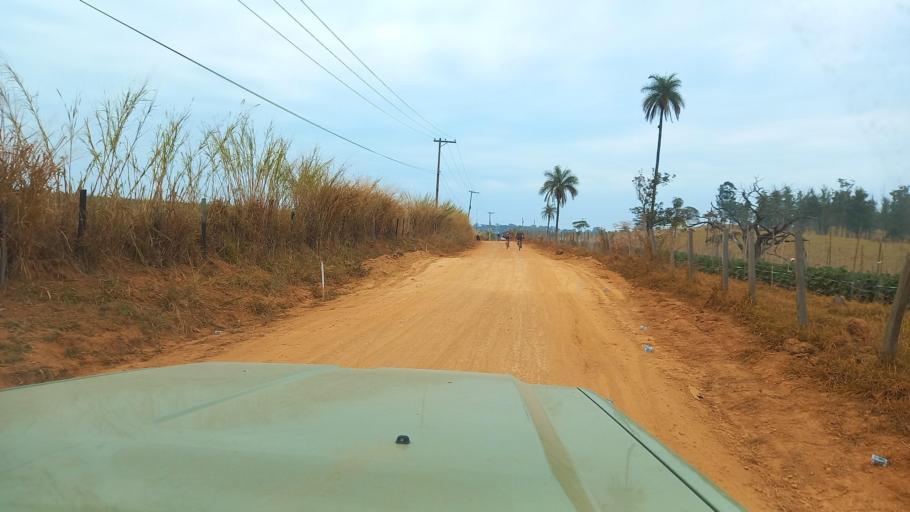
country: BR
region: Sao Paulo
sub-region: Moji-Guacu
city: Mogi-Gaucu
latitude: -22.3120
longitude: -46.8381
